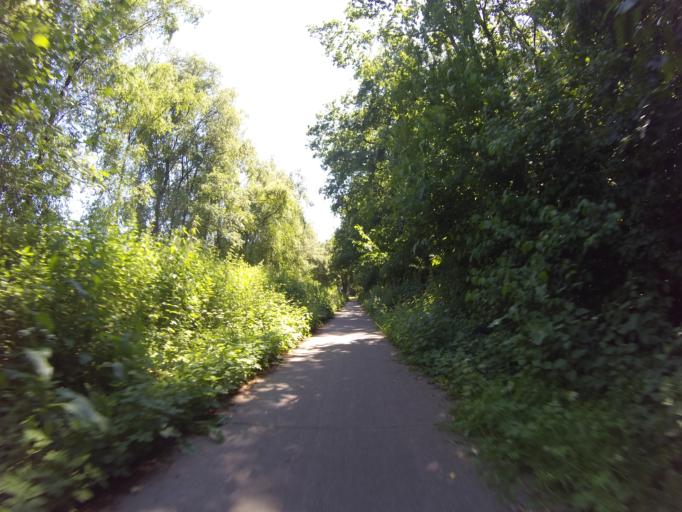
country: NL
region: Drenthe
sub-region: Gemeente Emmen
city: Emmen
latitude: 52.8013
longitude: 6.9289
